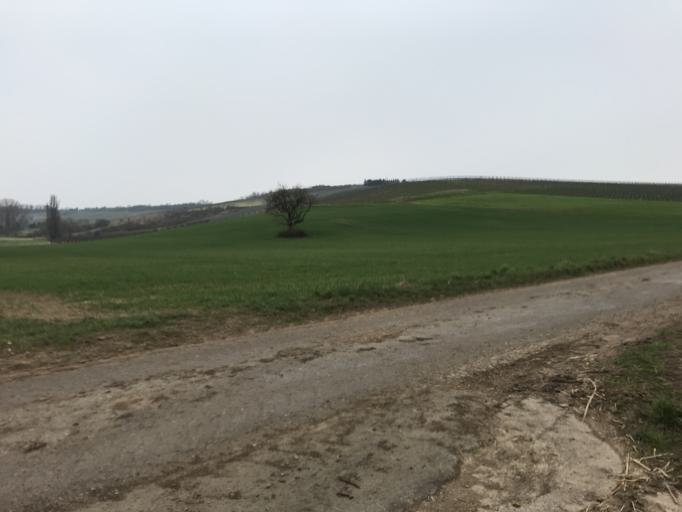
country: DE
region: Rheinland-Pfalz
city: Ober-Olm
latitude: 49.9278
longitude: 8.1821
